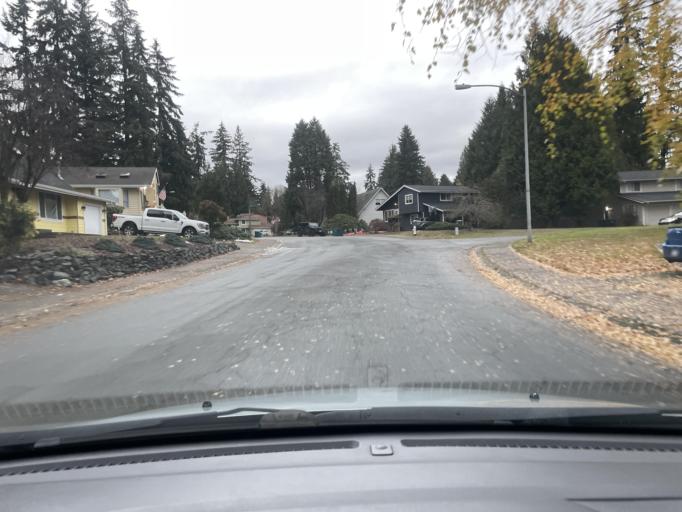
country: US
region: Washington
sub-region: King County
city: Kingsgate
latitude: 47.7231
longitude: -122.1789
